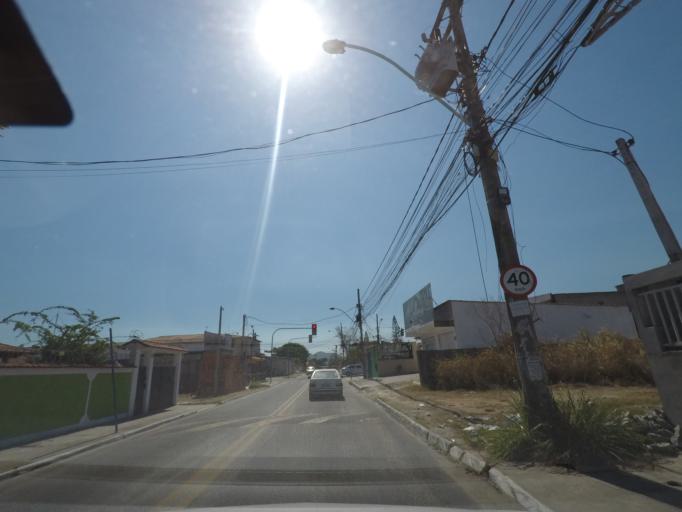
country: BR
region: Rio de Janeiro
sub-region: Marica
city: Marica
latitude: -22.9670
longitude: -42.9419
